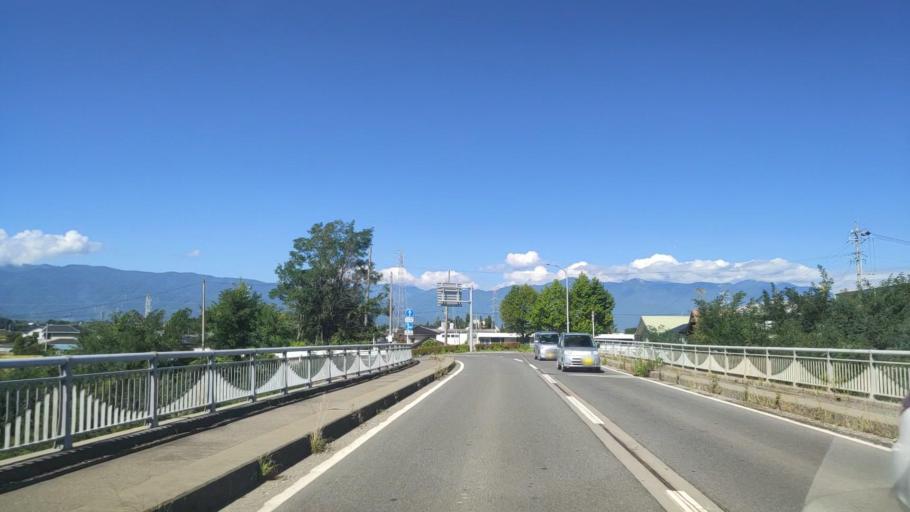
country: JP
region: Nagano
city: Shiojiri
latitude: 36.1644
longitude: 137.9441
